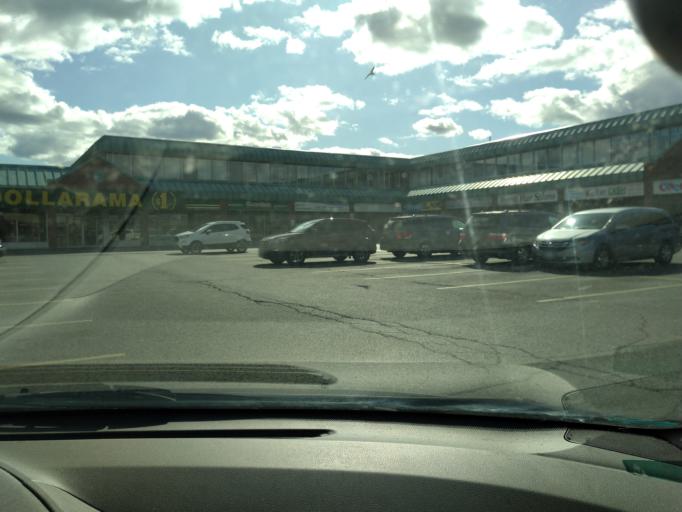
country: CA
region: Ontario
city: Newmarket
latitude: 44.0548
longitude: -79.4758
